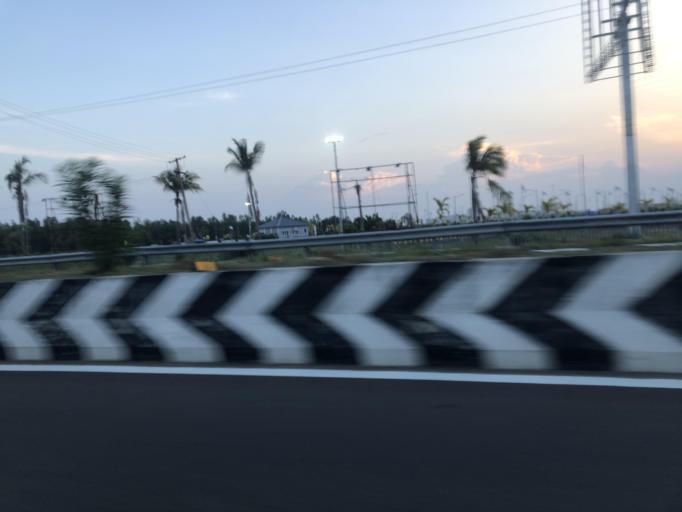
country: IN
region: Tamil Nadu
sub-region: Kancheepuram
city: Injambakkam
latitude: 12.7894
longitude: 80.2429
